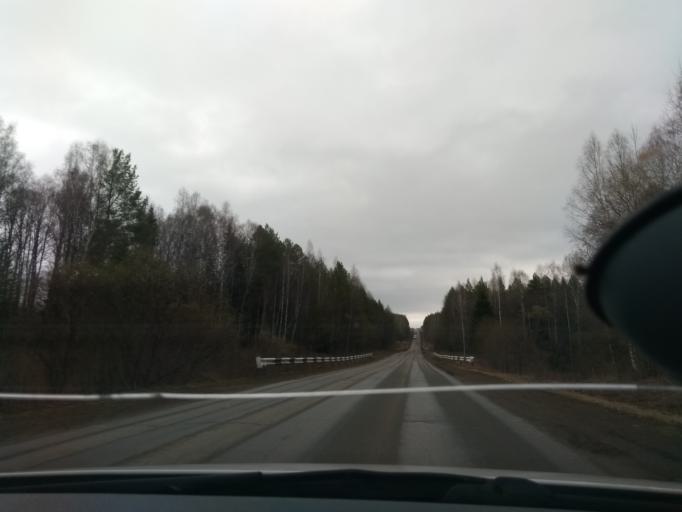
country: RU
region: Perm
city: Kungur
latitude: 57.3690
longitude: 56.8306
